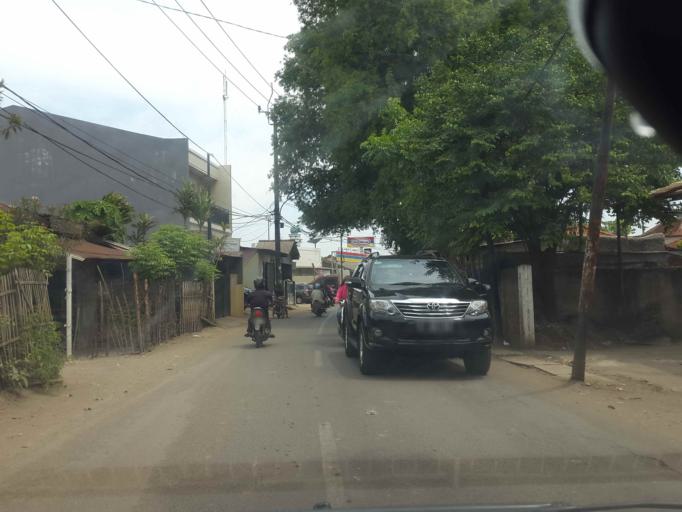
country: ID
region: Banten
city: Tangerang
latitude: -6.1543
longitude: 106.6276
